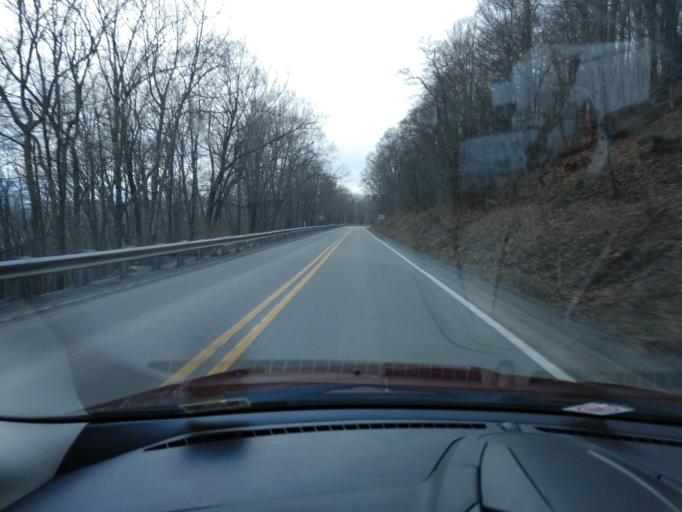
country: US
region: West Virginia
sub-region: Randolph County
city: Elkins
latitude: 38.6340
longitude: -79.9277
